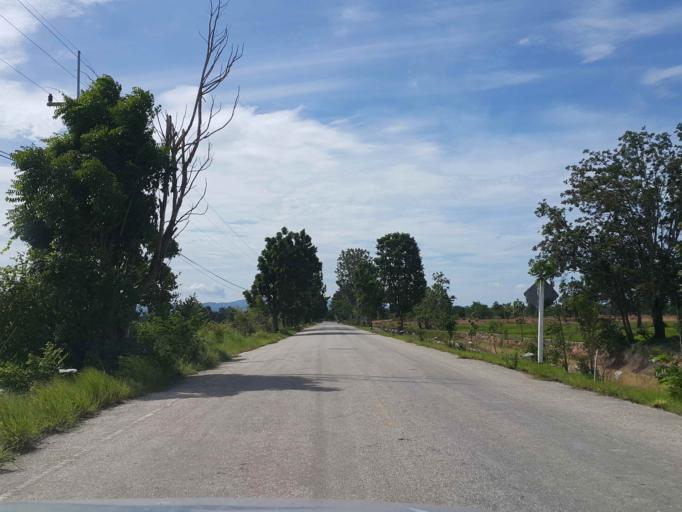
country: TH
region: Sukhothai
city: Ban Dan Lan Hoi
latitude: 17.1342
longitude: 99.5266
